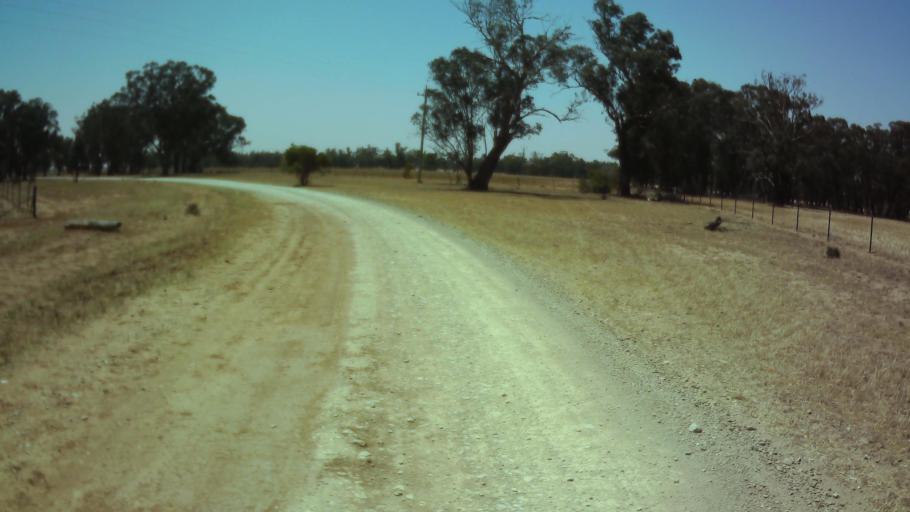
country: AU
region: New South Wales
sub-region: Weddin
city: Grenfell
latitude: -34.0206
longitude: 147.9004
